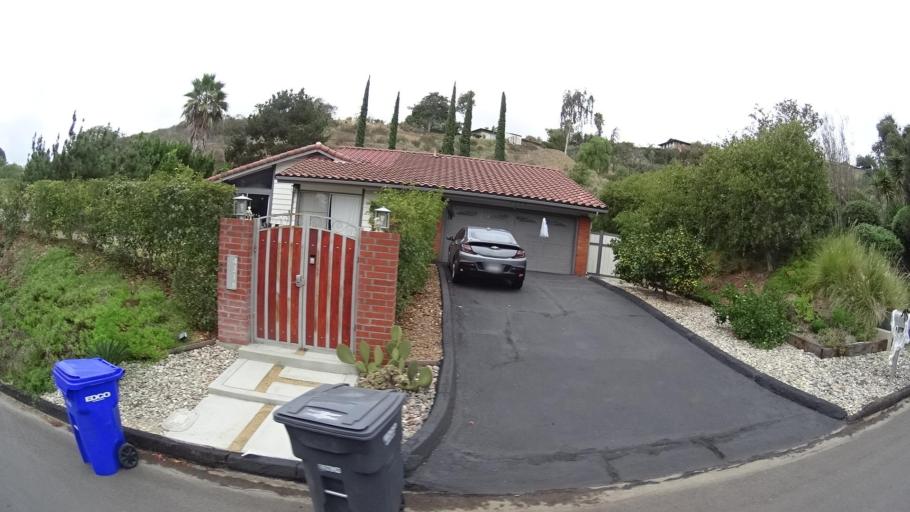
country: US
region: California
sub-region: San Diego County
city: Spring Valley
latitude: 32.7596
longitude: -116.9881
